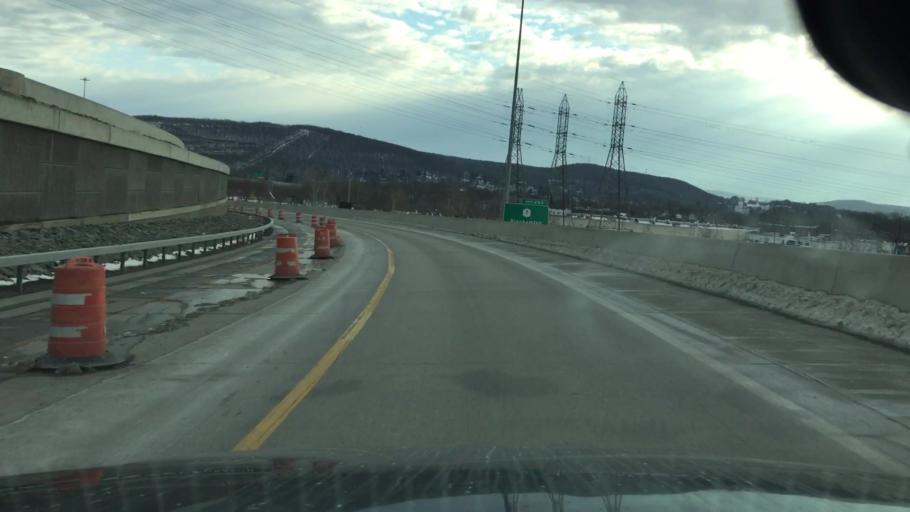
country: US
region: New York
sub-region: Broome County
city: Binghamton
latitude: 42.1116
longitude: -75.9131
